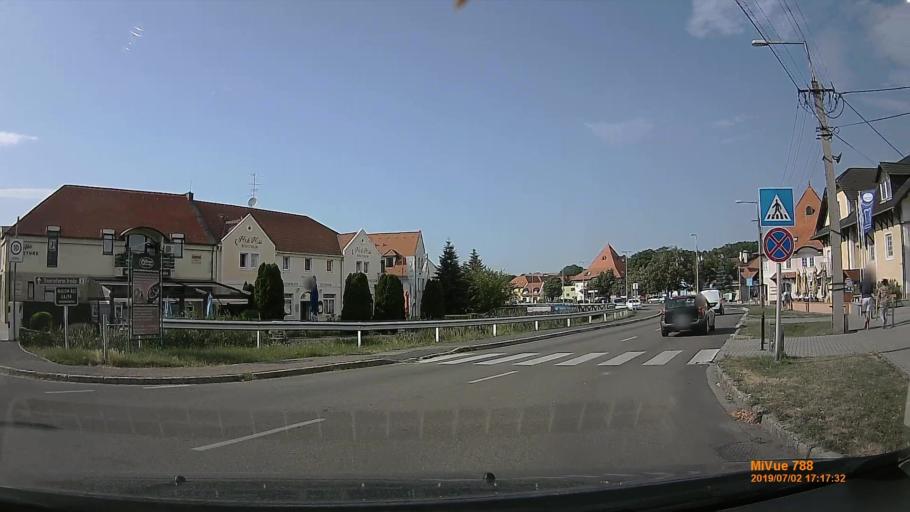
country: HU
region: Gyor-Moson-Sopron
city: Mosonmagyarovar
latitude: 47.8759
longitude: 17.2736
